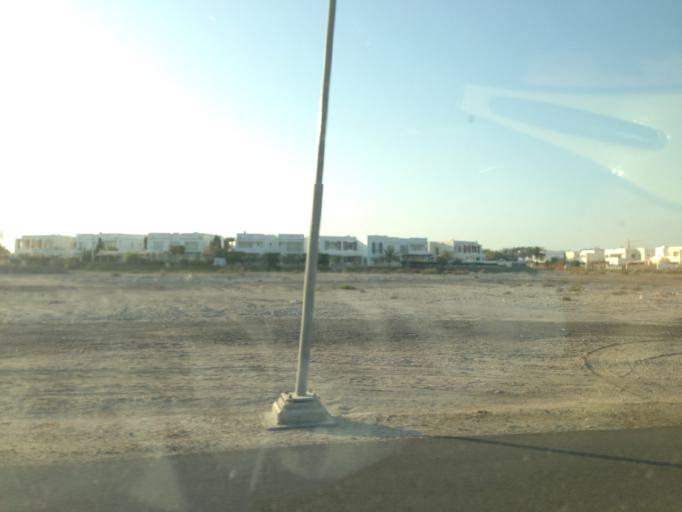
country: OM
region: Muhafazat Masqat
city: As Sib al Jadidah
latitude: 23.6214
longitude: 58.2733
